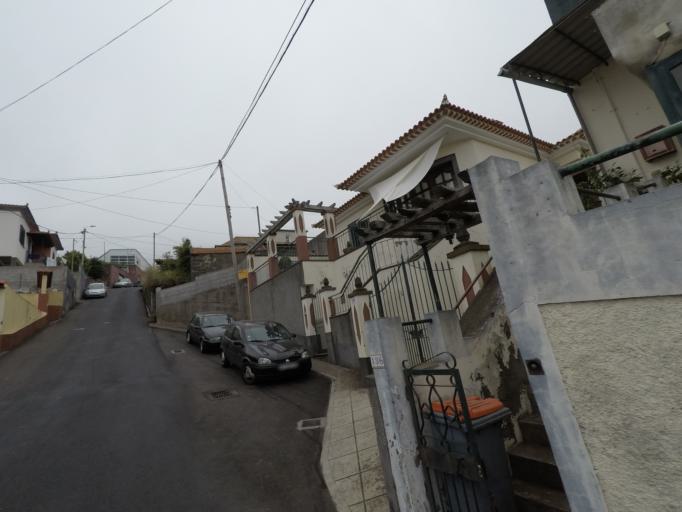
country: PT
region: Madeira
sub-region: Camara de Lobos
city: Curral das Freiras
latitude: 32.6844
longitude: -16.9471
